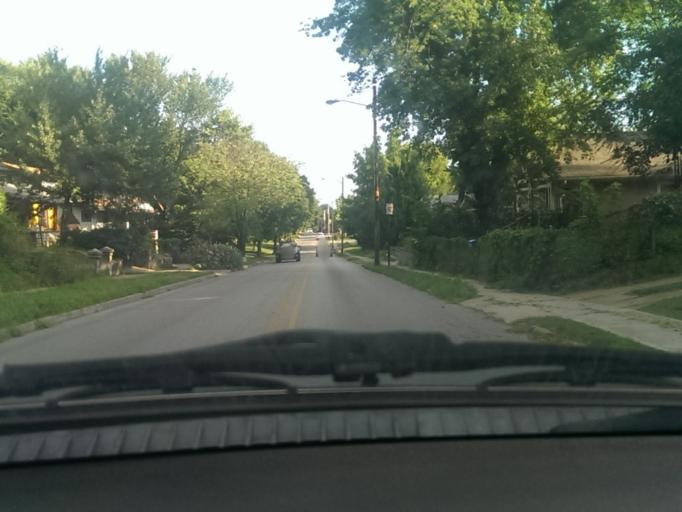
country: US
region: Kansas
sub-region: Johnson County
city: Westwood
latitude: 39.0484
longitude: -94.6074
